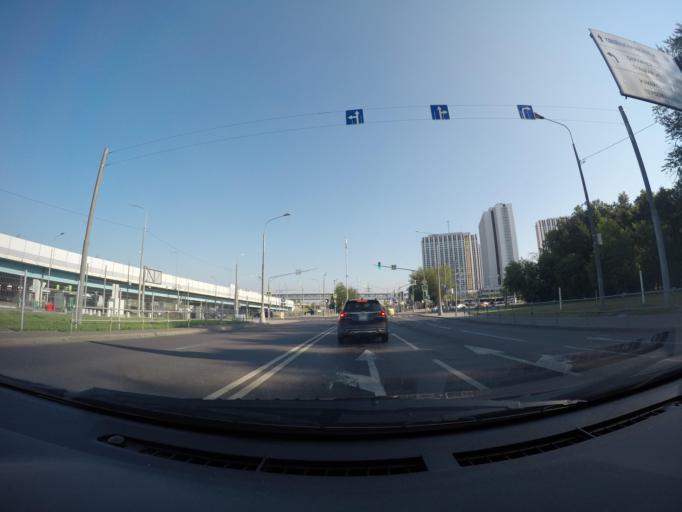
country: RU
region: Moskovskaya
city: Bogorodskoye
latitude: 55.7867
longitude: 37.7456
